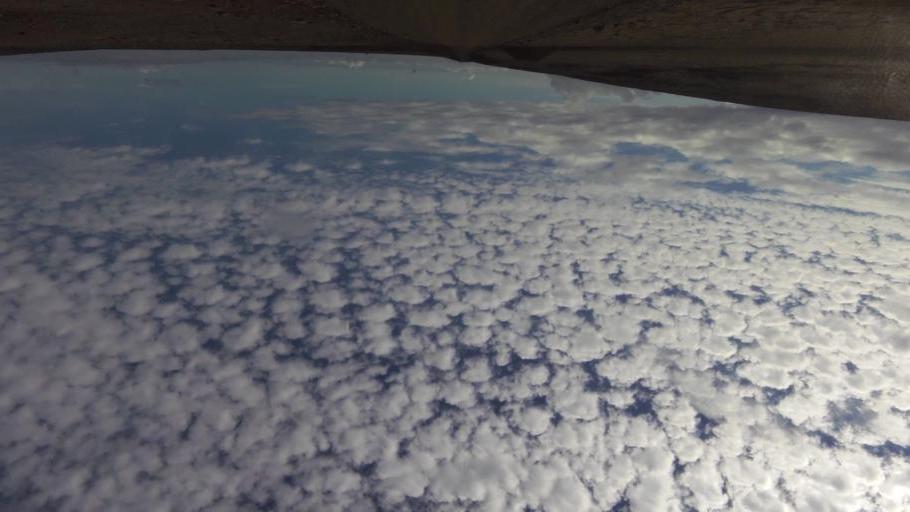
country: IS
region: West
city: Olafsvik
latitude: 65.6184
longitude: -24.2594
